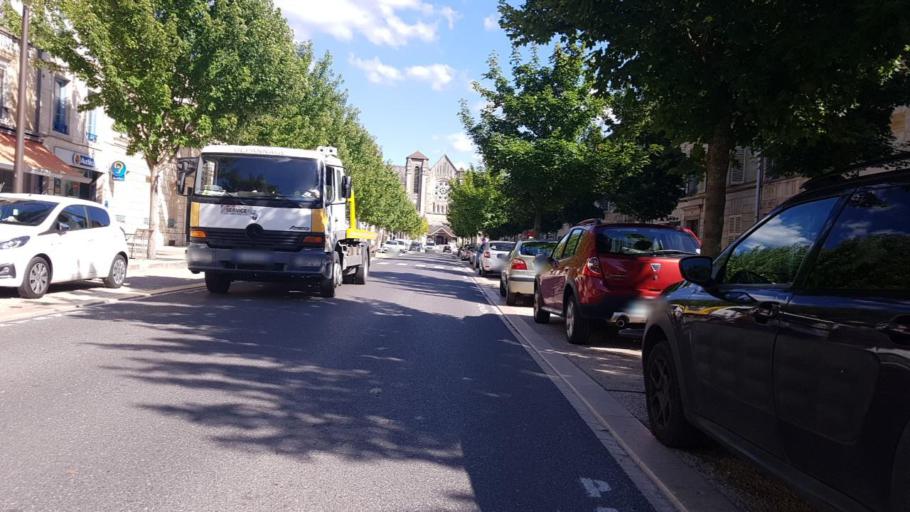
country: FR
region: Lorraine
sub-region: Departement de la Meuse
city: Bar-le-Duc
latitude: 48.7713
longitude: 5.1643
